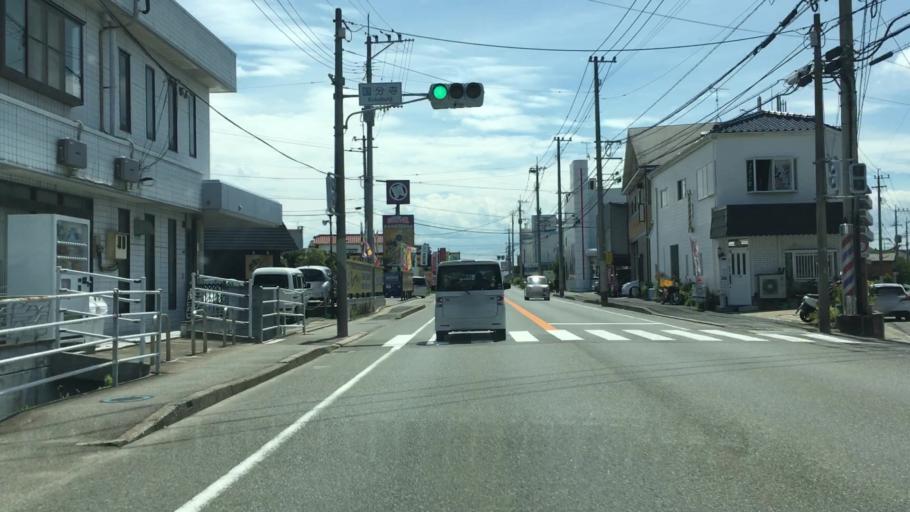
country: JP
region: Fukuoka
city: Dazaifu
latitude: 33.5177
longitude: 130.5025
